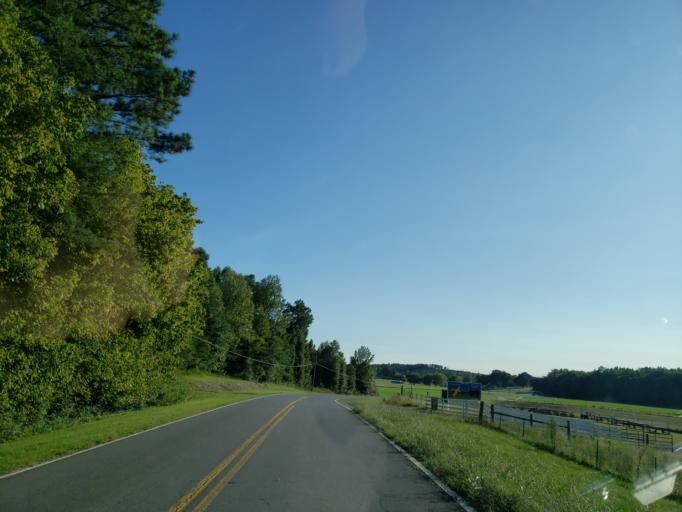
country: US
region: Georgia
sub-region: Bartow County
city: Rydal
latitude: 34.3170
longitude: -84.7680
